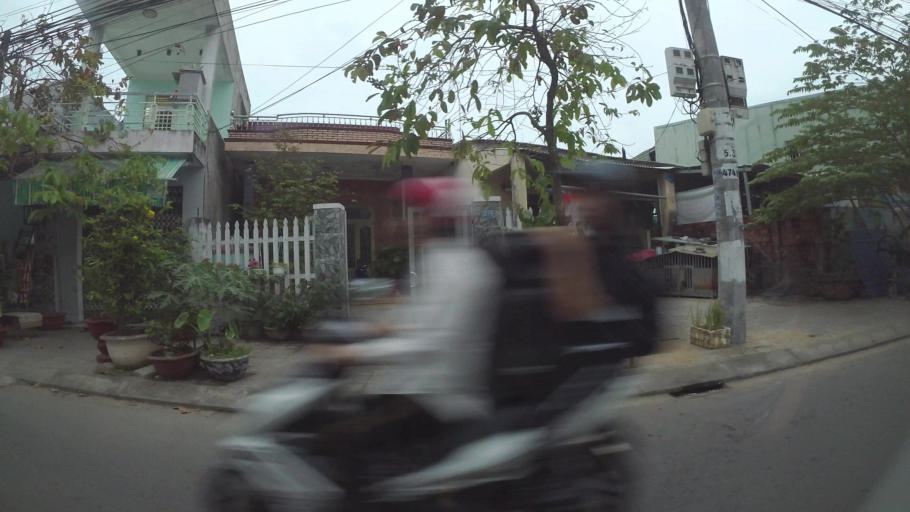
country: VN
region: Da Nang
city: Thanh Khe
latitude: 16.0491
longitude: 108.1765
